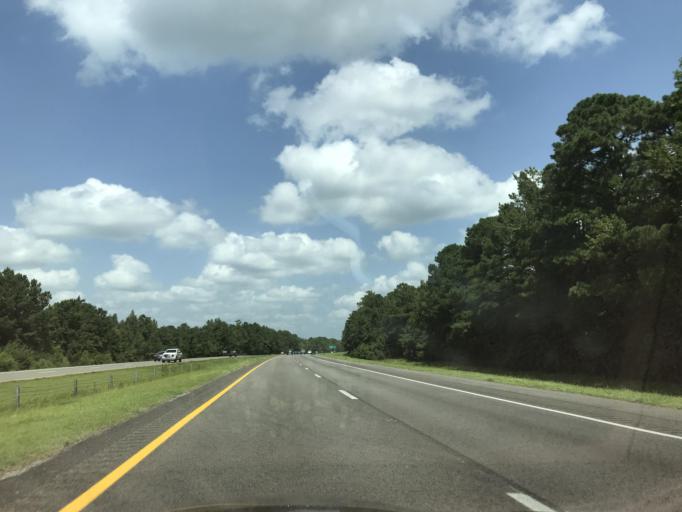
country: US
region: North Carolina
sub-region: Pender County
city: Rocky Point
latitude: 34.4606
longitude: -77.8796
